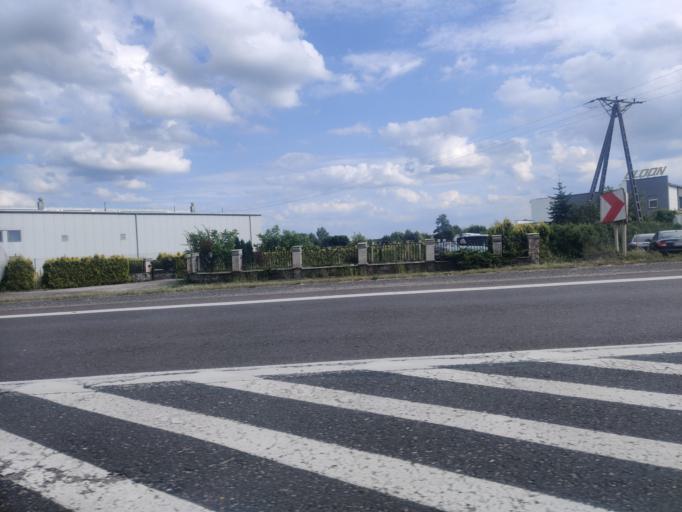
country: PL
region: Greater Poland Voivodeship
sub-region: Konin
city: Konin
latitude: 52.1929
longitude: 18.2662
